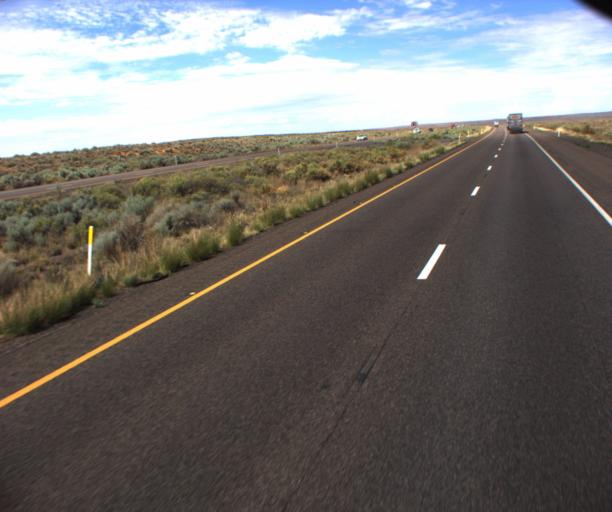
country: US
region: Arizona
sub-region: Apache County
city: Houck
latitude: 35.0947
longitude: -109.6728
